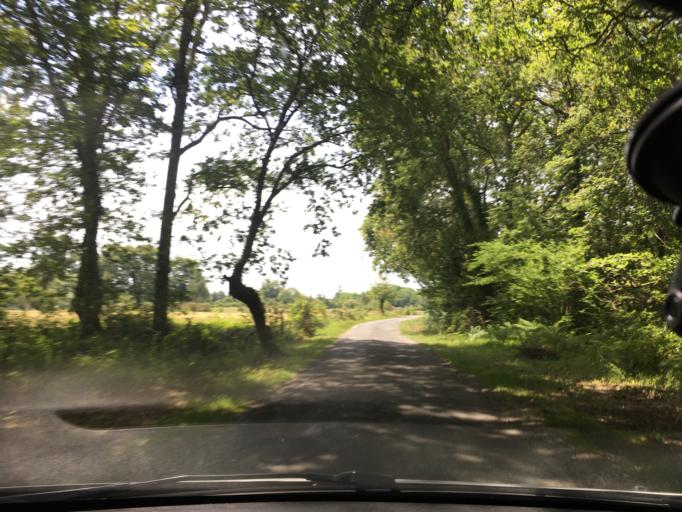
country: FR
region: Aquitaine
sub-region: Departement de la Gironde
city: Lesparre-Medoc
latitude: 45.2784
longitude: -0.9112
